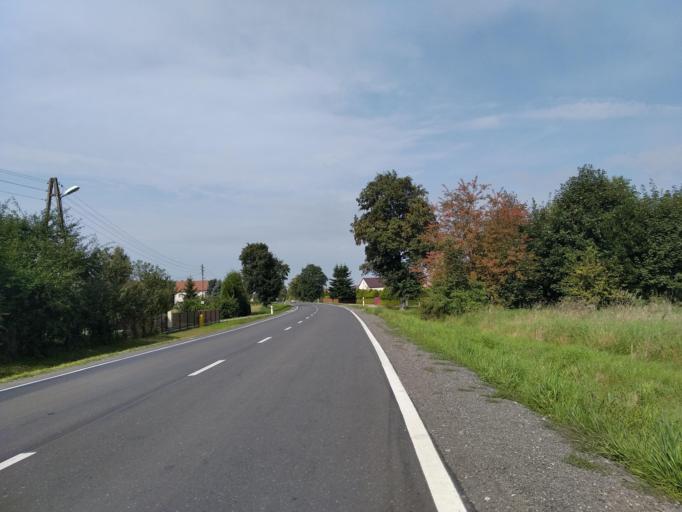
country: PL
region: Subcarpathian Voivodeship
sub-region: Powiat mielecki
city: Przeclaw
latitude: 50.1681
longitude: 21.5020
